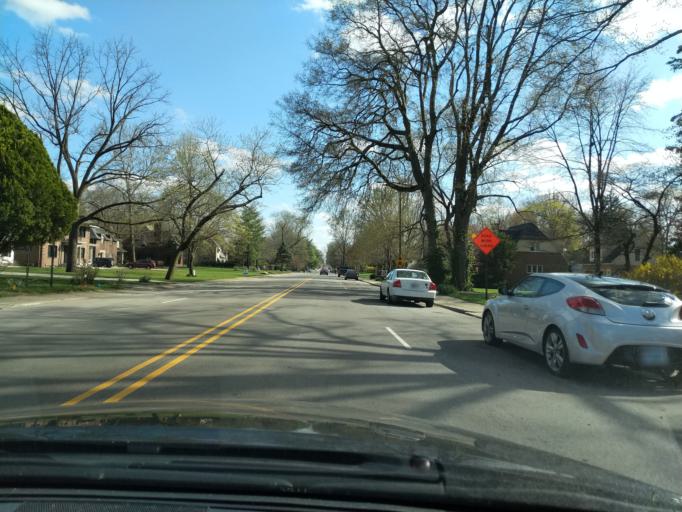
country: US
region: Indiana
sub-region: Marion County
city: Broad Ripple
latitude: 39.8612
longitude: -86.1502
